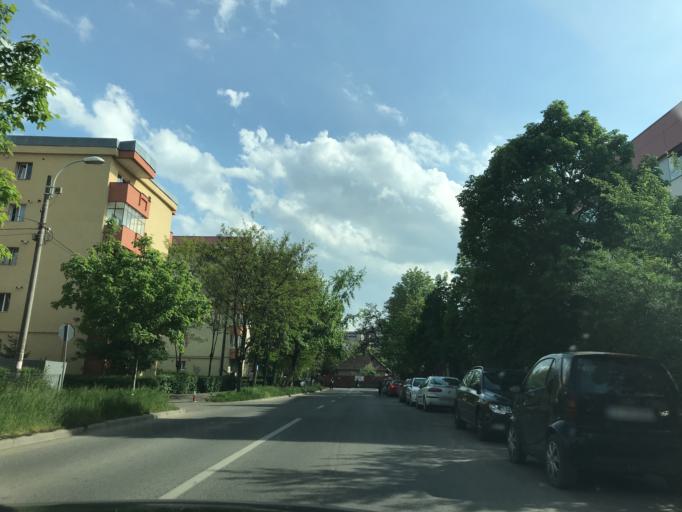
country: RO
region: Cluj
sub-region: Municipiul Cluj-Napoca
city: Cluj-Napoca
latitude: 46.7836
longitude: 23.6151
